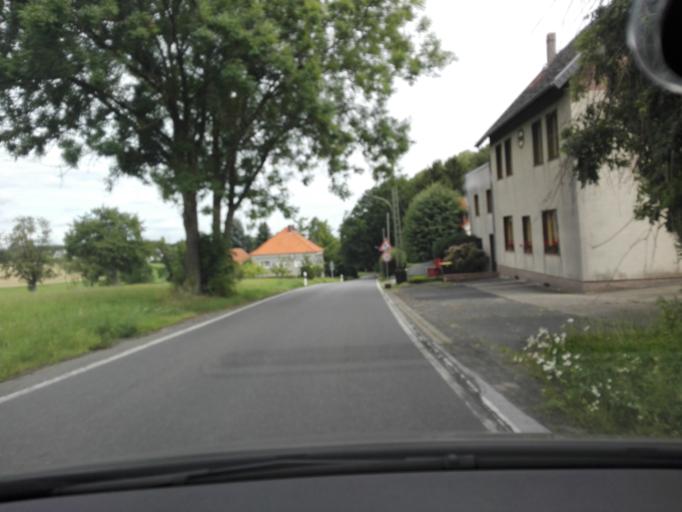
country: DE
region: North Rhine-Westphalia
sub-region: Regierungsbezirk Arnsberg
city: Unna
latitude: 51.5151
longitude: 7.7271
